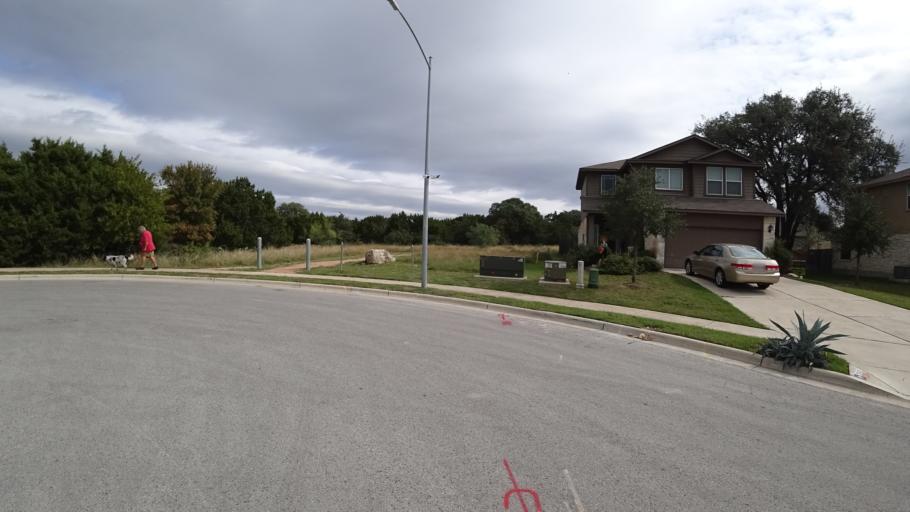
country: US
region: Texas
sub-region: Travis County
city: Shady Hollow
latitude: 30.1550
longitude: -97.8473
